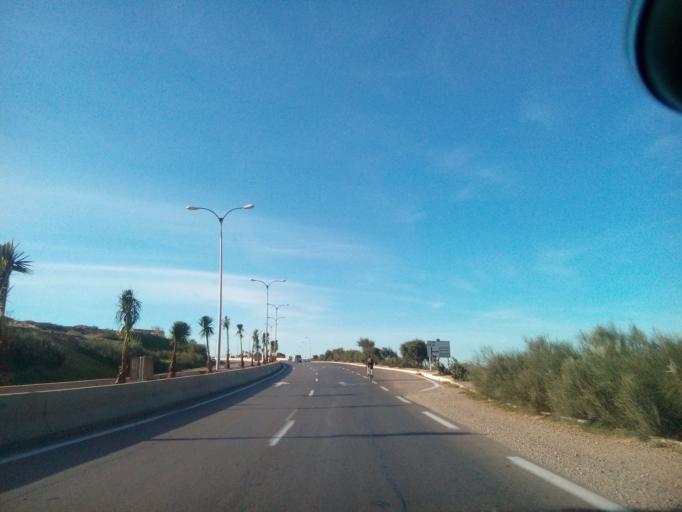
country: DZ
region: Mostaganem
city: Mostaganem
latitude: 35.8355
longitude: -0.0069
